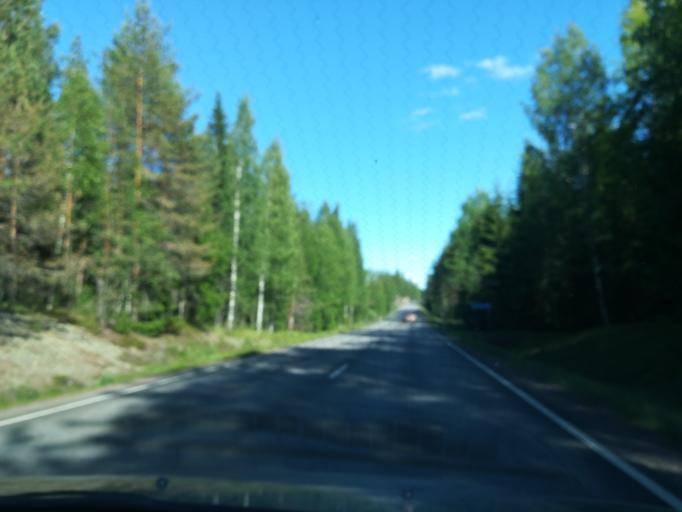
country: FI
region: South Karelia
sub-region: Imatra
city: Ruokolahti
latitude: 61.3646
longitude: 28.6912
